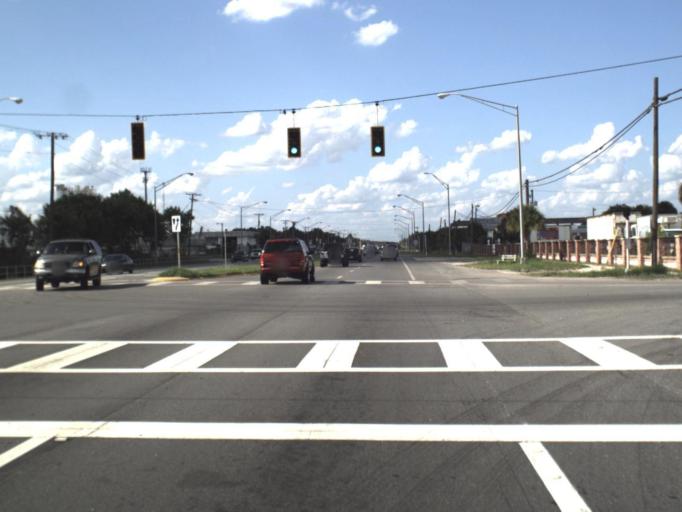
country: US
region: Florida
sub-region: Hillsborough County
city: East Lake-Orient Park
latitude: 28.0032
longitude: -82.3934
